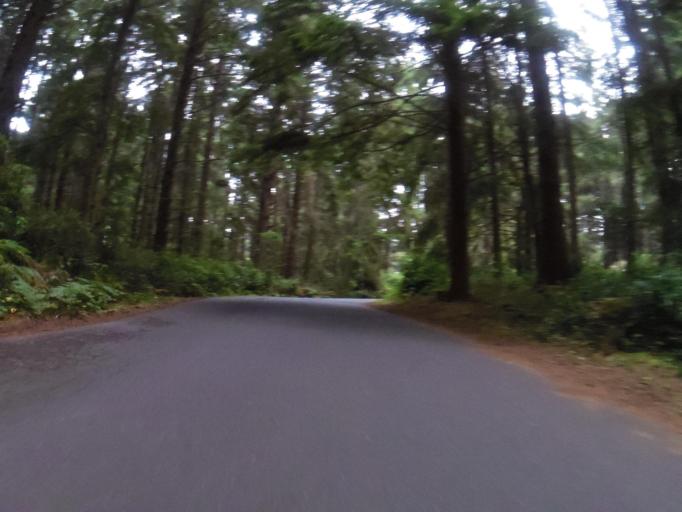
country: US
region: California
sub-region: Humboldt County
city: Westhaven-Moonstone
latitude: 41.1370
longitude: -124.1590
